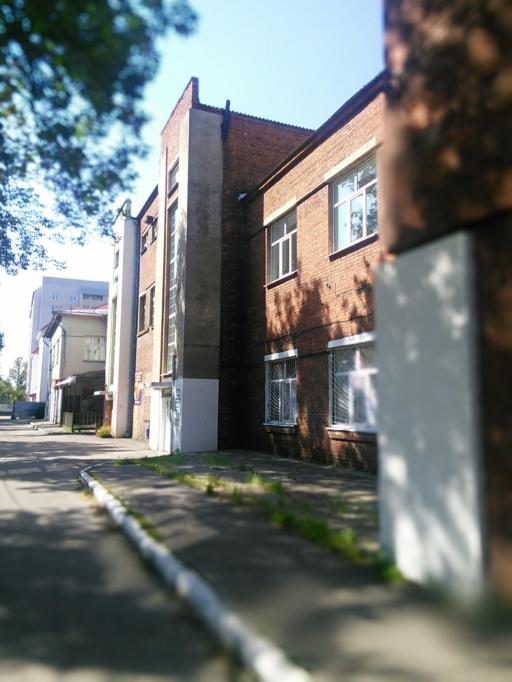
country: RU
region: Jaroslavl
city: Yaroslavl
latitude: 57.6114
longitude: 39.8234
